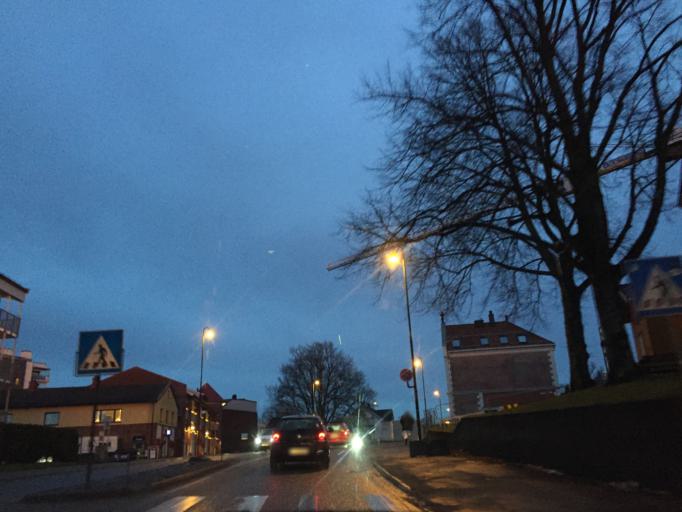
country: NO
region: Ostfold
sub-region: Moss
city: Moss
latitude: 59.4340
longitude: 10.6644
